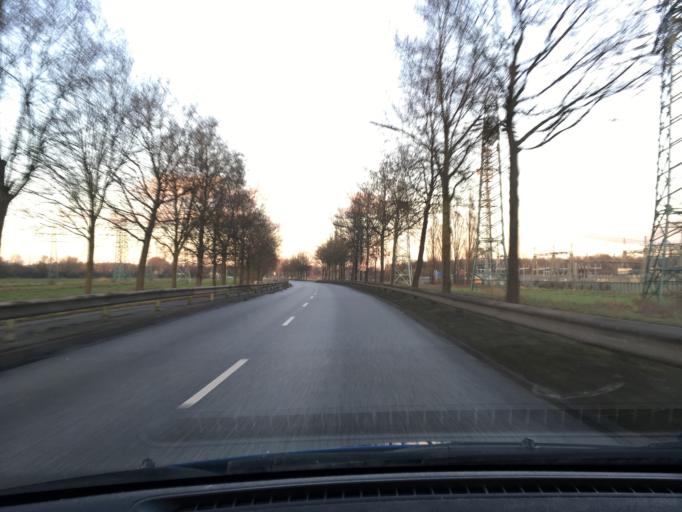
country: DE
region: Hamburg
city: Altona
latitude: 53.4878
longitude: 9.9055
